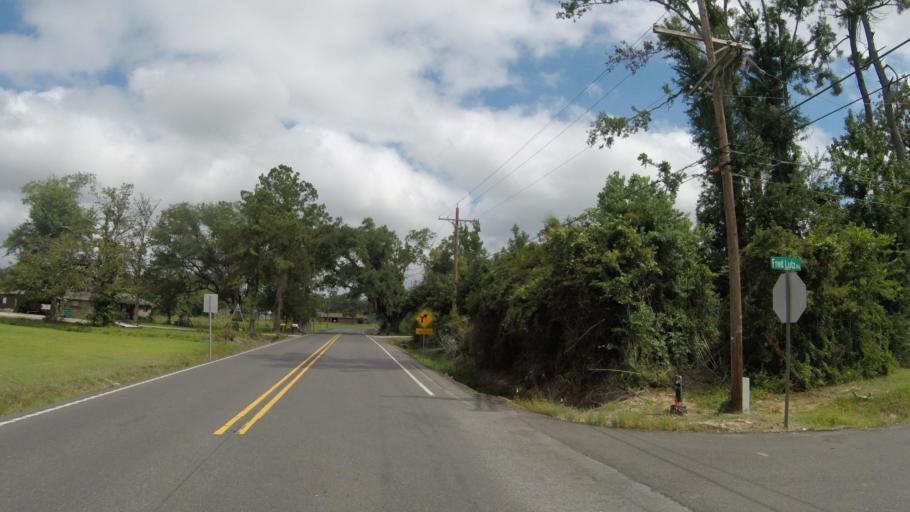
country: US
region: Louisiana
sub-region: Calcasieu Parish
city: Westlake
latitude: 30.2629
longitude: -93.2457
